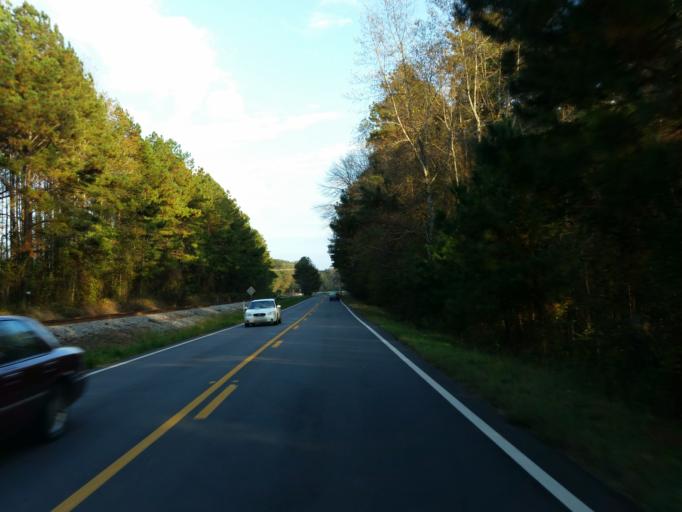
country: US
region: Georgia
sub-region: Monroe County
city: Forsyth
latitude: 32.9538
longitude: -83.8565
